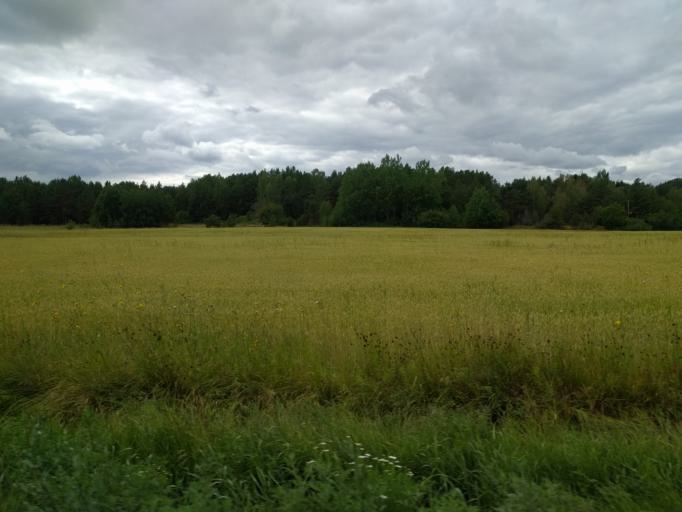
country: SE
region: Soedermanland
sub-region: Nykopings Kommun
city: Svalsta
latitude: 58.4973
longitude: 16.8813
